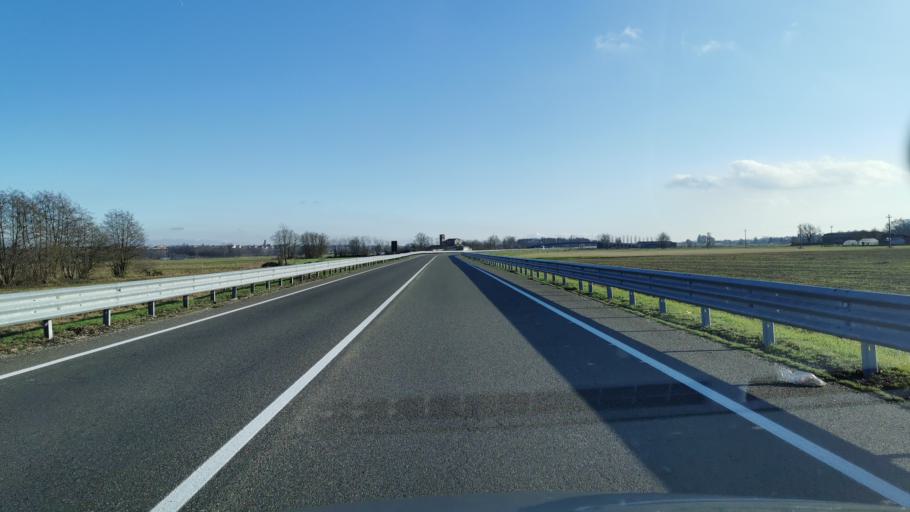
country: IT
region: Piedmont
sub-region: Provincia di Biella
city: Castelletto Cervo
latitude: 45.5248
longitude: 8.1995
